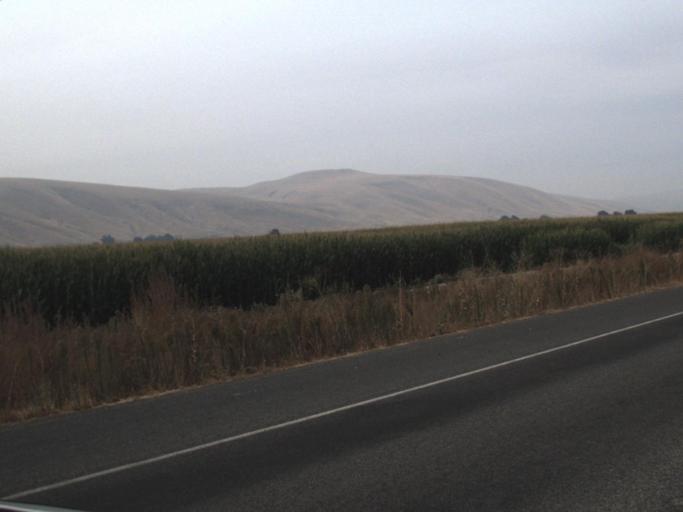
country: US
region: Washington
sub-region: Yakima County
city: Granger
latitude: 46.3277
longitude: -120.2417
